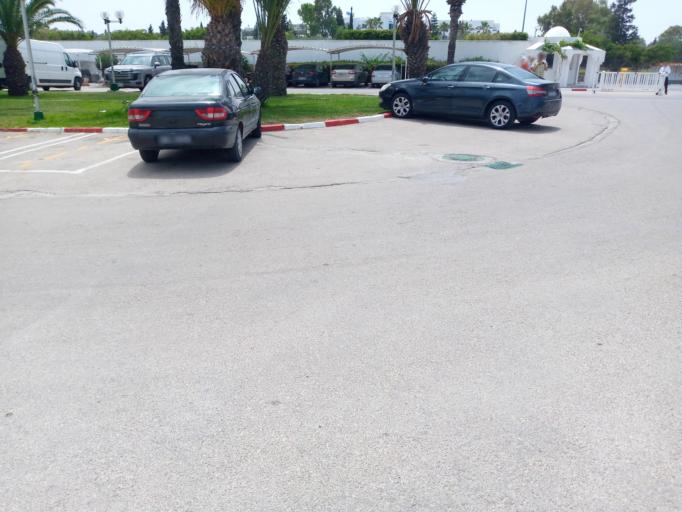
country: TN
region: Susah
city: Port el Kantaoui
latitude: 35.9034
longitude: 10.5835
